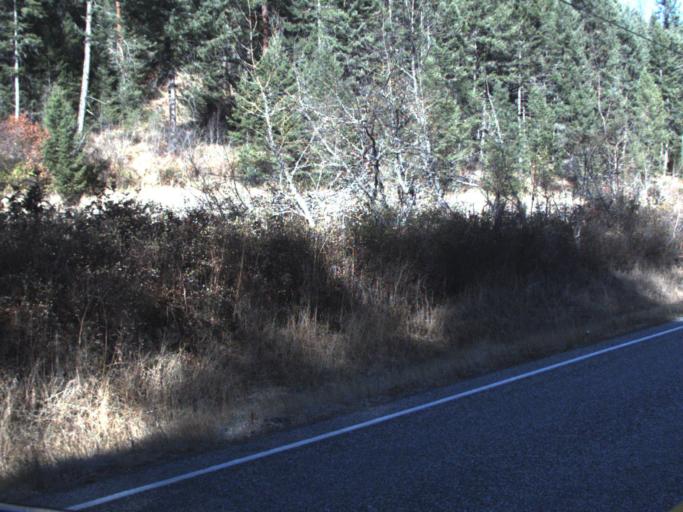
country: CA
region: British Columbia
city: Grand Forks
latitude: 48.9702
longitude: -118.5270
